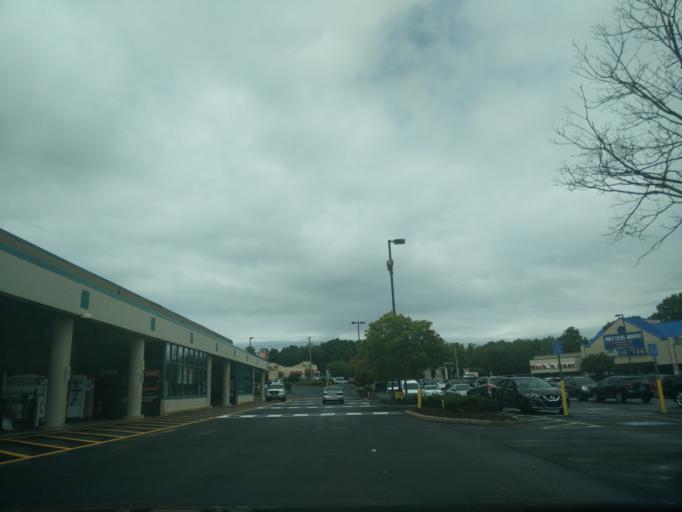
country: US
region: Connecticut
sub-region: New Haven County
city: Orange
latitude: 41.2574
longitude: -73.0108
